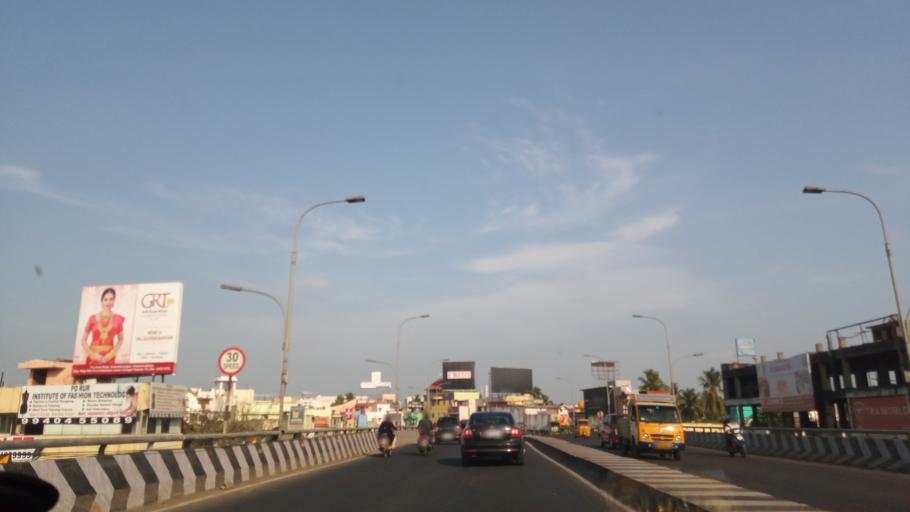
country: IN
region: Tamil Nadu
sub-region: Thiruvallur
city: Porur
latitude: 13.0348
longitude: 80.1558
